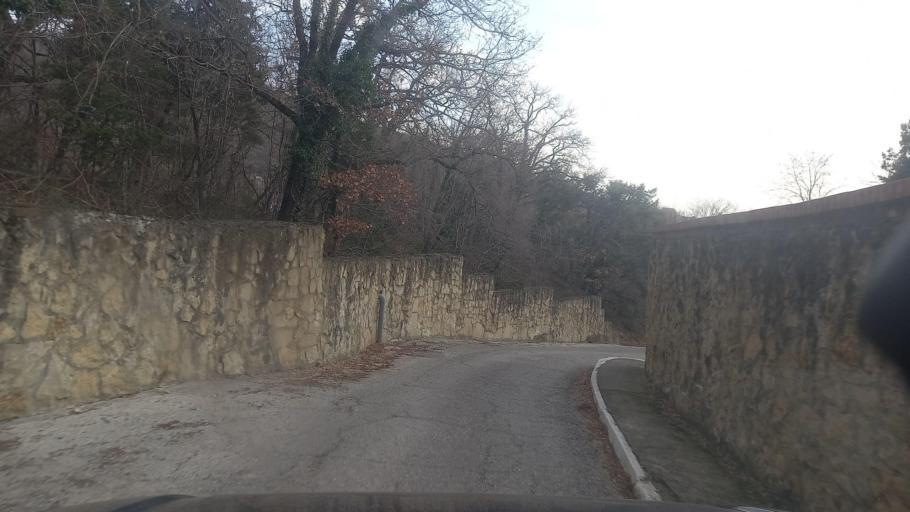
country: RU
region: Krasnodarskiy
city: Myskhako
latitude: 44.6654
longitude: 37.6841
